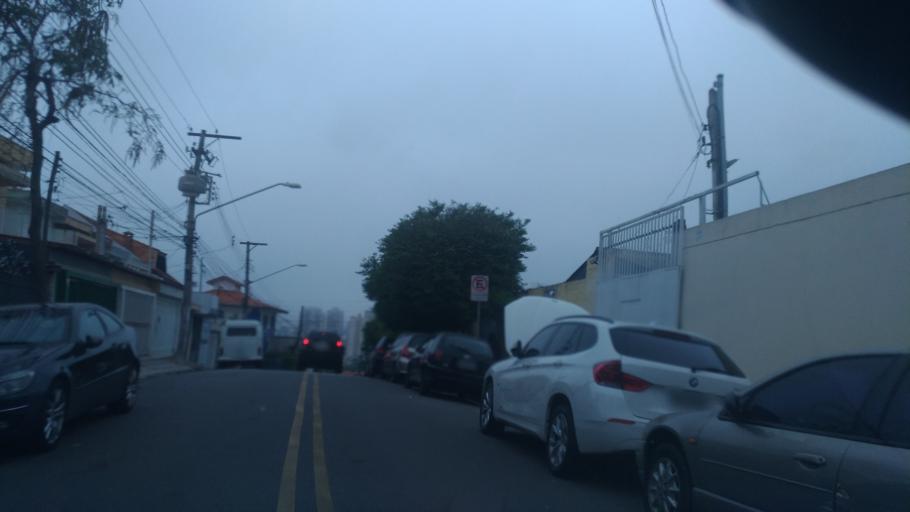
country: BR
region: Sao Paulo
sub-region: Sao Bernardo Do Campo
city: Sao Bernardo do Campo
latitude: -23.6969
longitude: -46.5584
